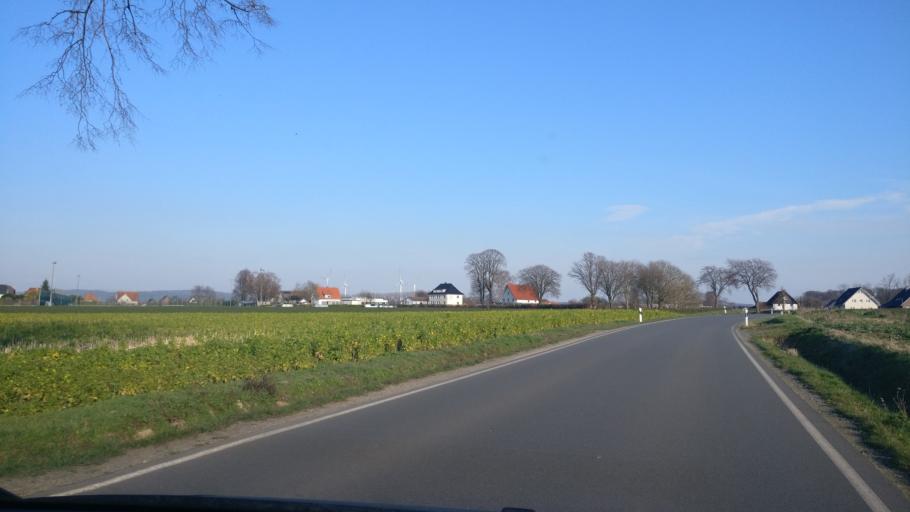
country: DE
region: North Rhine-Westphalia
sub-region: Regierungsbezirk Detmold
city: Lage
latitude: 52.0162
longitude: 8.7803
